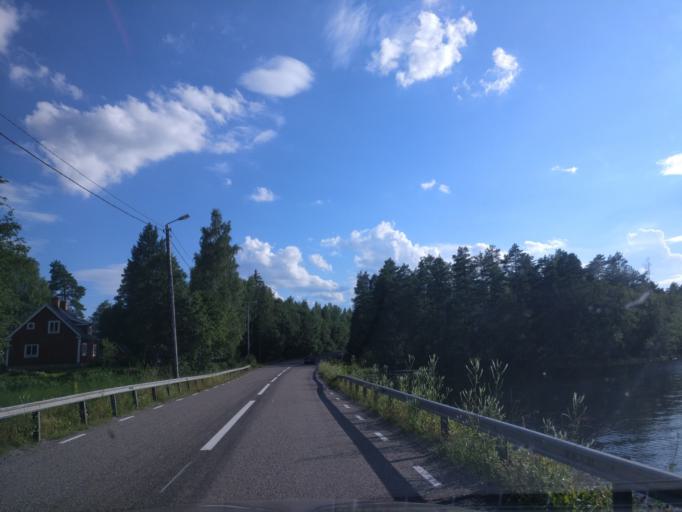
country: SE
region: Dalarna
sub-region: Ludvika Kommun
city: Ludvika
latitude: 60.2977
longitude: 15.2192
